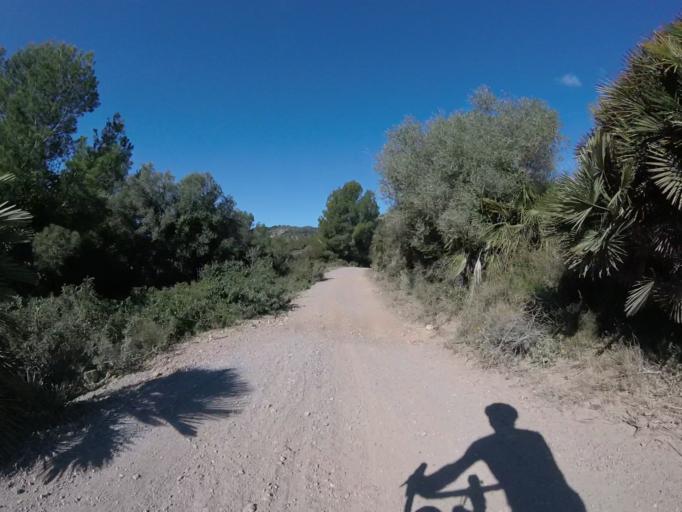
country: ES
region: Valencia
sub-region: Provincia de Castello
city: Benicassim
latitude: 40.0817
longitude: 0.0841
